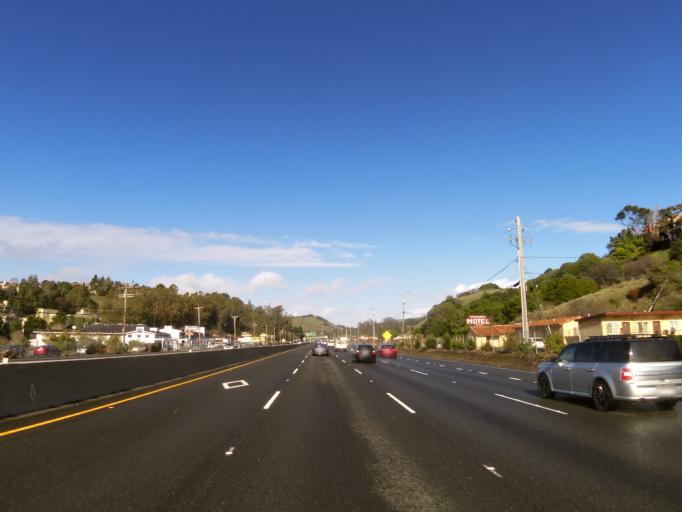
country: US
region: California
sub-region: Marin County
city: Strawberry
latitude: 37.8917
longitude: -122.5165
